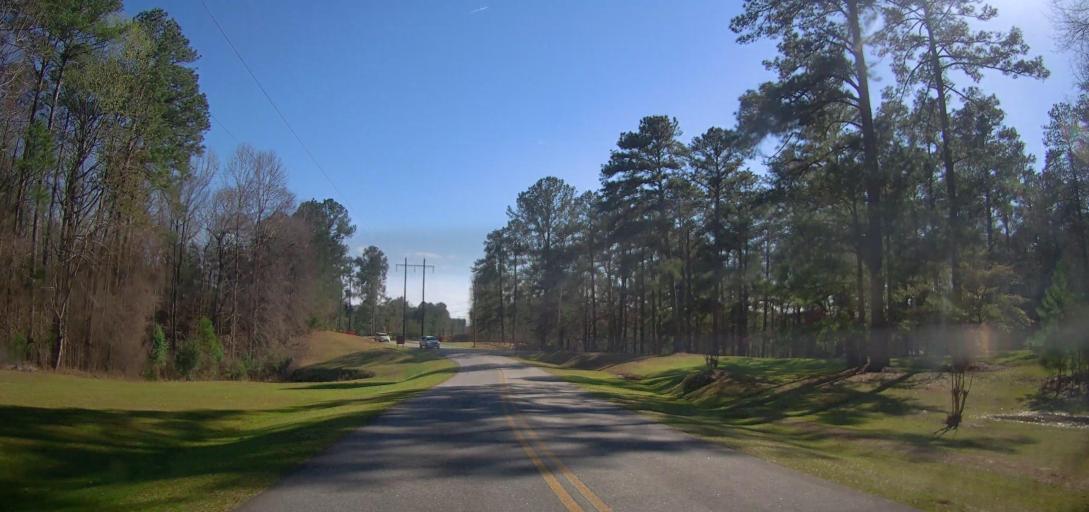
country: US
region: Georgia
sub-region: Butts County
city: Indian Springs
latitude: 33.2498
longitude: -83.9256
